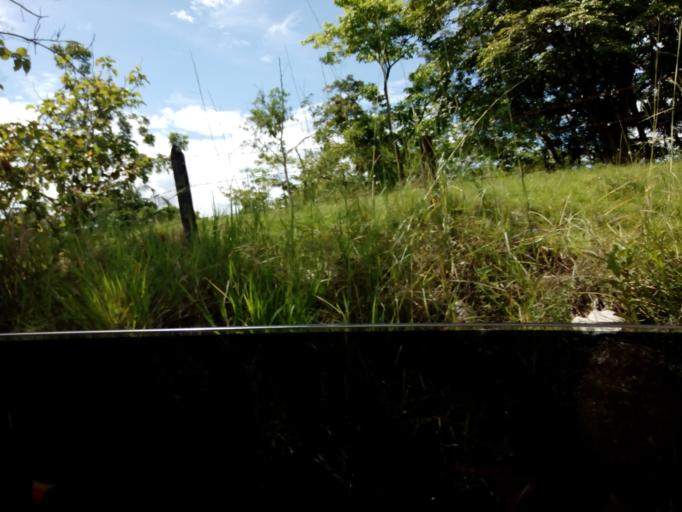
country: CO
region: Boyaca
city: Puerto Boyaca
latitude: 5.9558
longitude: -74.4676
